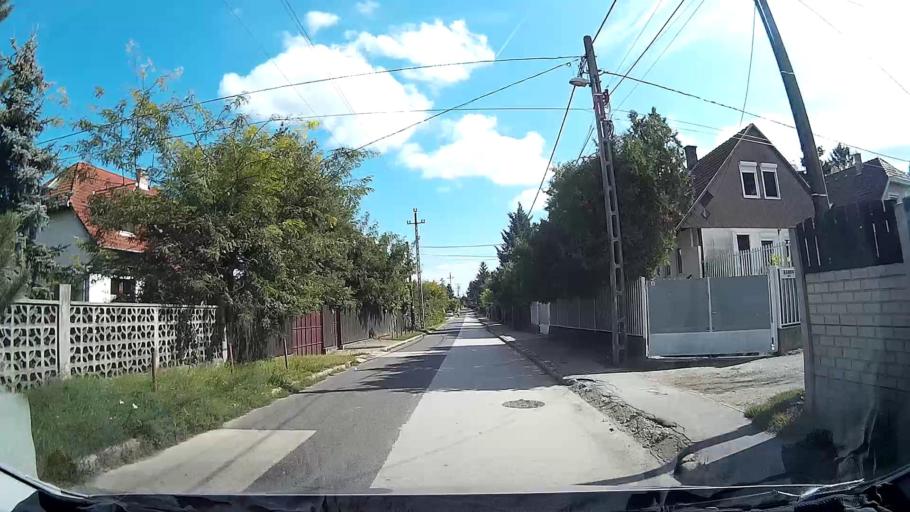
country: HU
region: Pest
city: Szentendre
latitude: 47.6786
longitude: 19.0724
